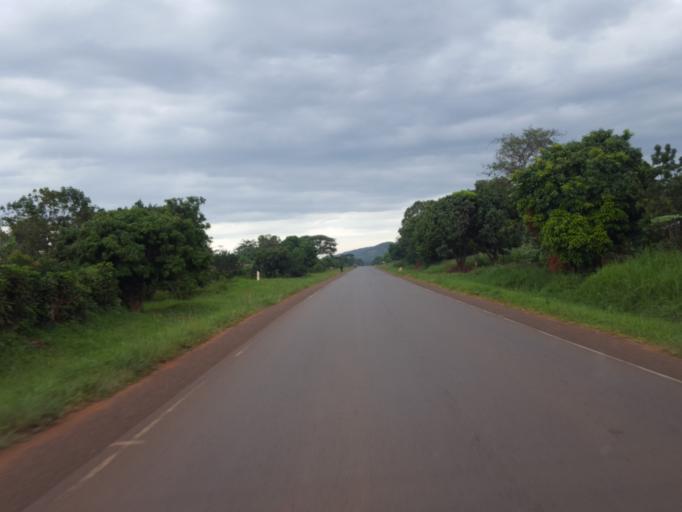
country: UG
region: Central Region
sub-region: Kiboga District
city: Kiboga
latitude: 0.8586
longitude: 31.8646
